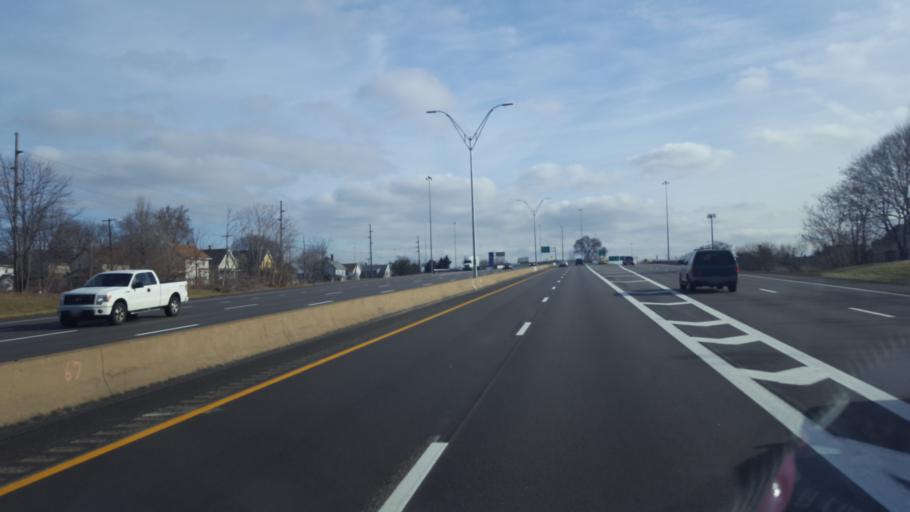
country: US
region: Ohio
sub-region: Stark County
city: Canton
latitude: 40.7844
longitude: -81.3914
